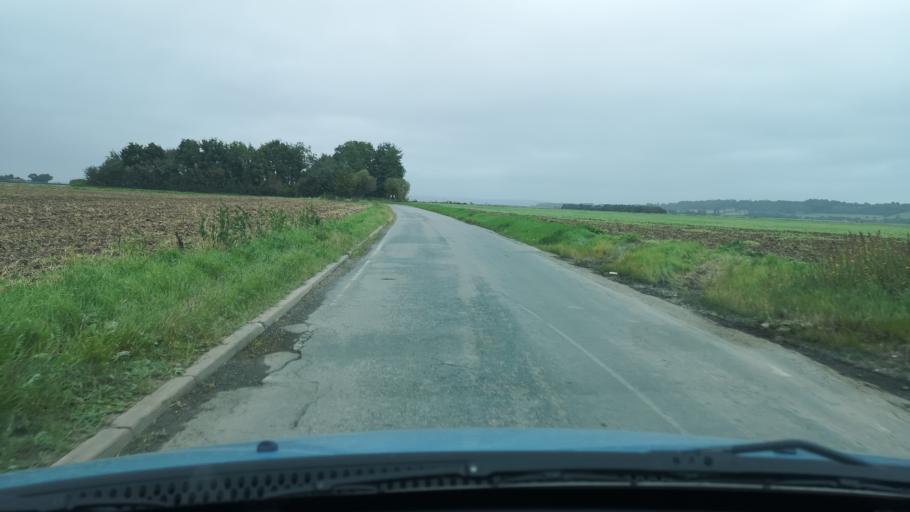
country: GB
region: England
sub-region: North Lincolnshire
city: Burton upon Stather
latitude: 53.6660
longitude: -0.7199
